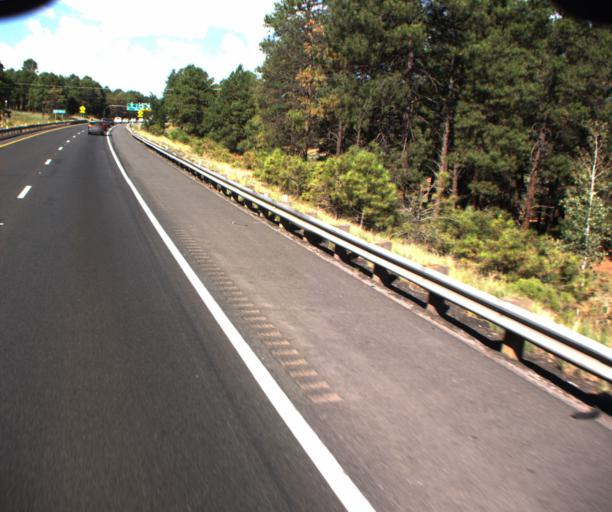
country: US
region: Arizona
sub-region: Coconino County
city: Flagstaff
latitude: 35.1741
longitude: -111.6467
